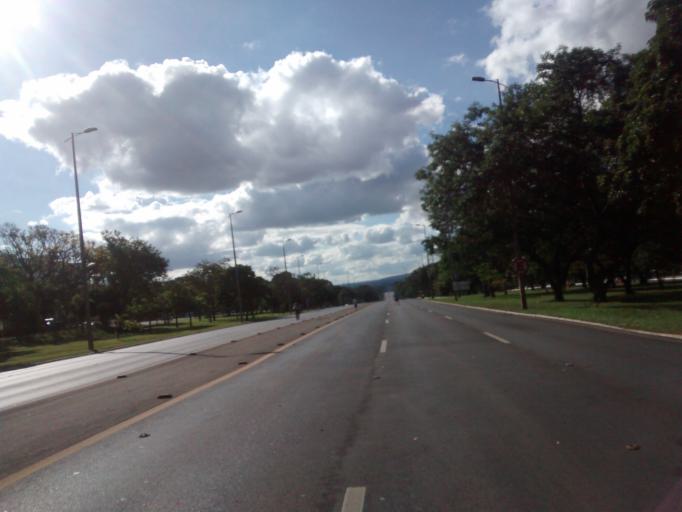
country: BR
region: Federal District
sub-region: Brasilia
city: Brasilia
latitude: -15.7610
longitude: -47.8844
